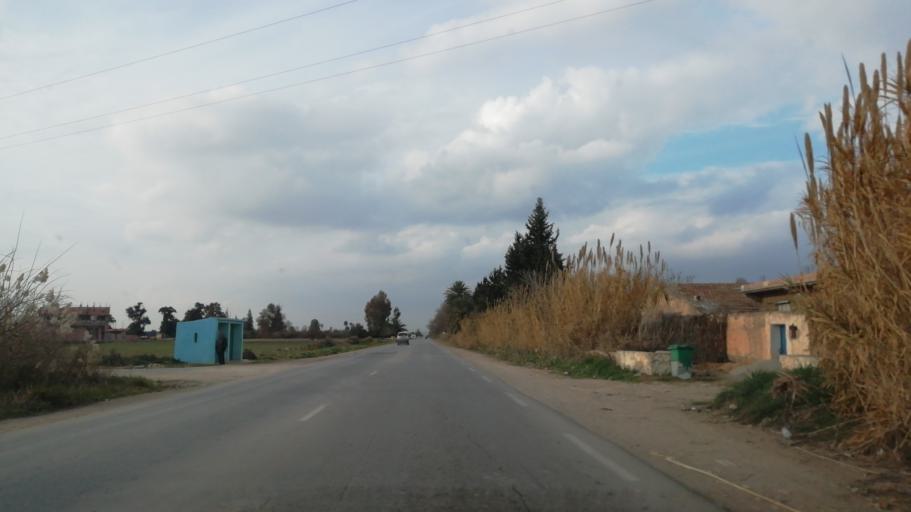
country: DZ
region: Mascara
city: Sig
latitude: 35.6803
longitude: -0.0101
